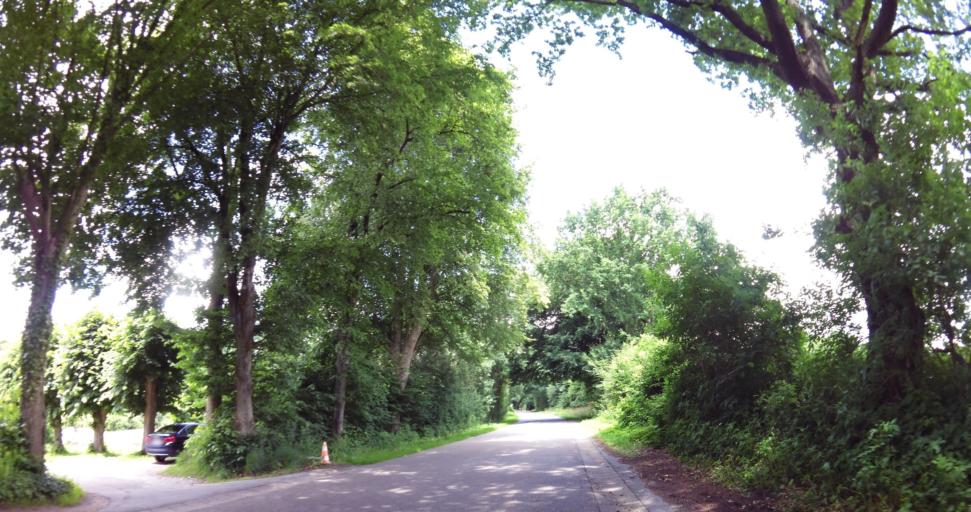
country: DE
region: Schleswig-Holstein
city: Fleckeby
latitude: 54.4976
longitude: 9.7296
